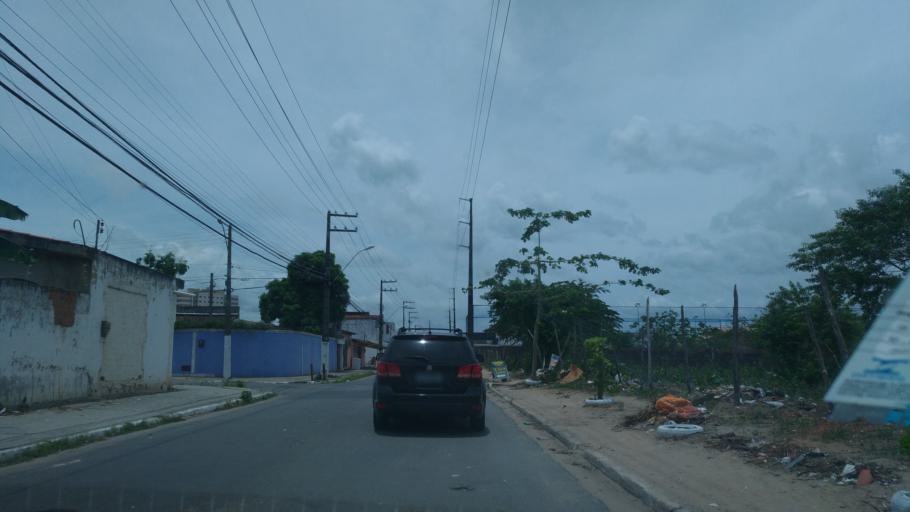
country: BR
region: Alagoas
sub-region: Satuba
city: Satuba
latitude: -9.5641
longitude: -35.7425
